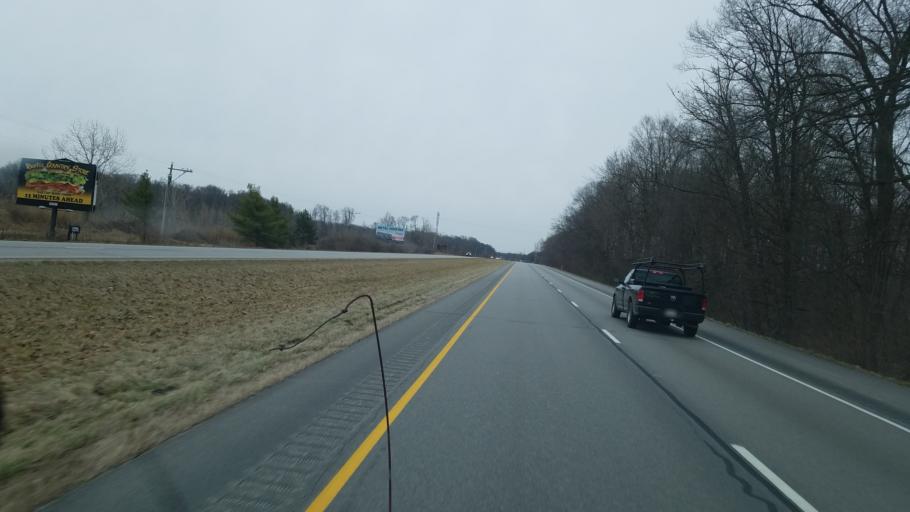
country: US
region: Indiana
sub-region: Marshall County
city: Plymouth
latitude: 41.3107
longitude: -86.2755
